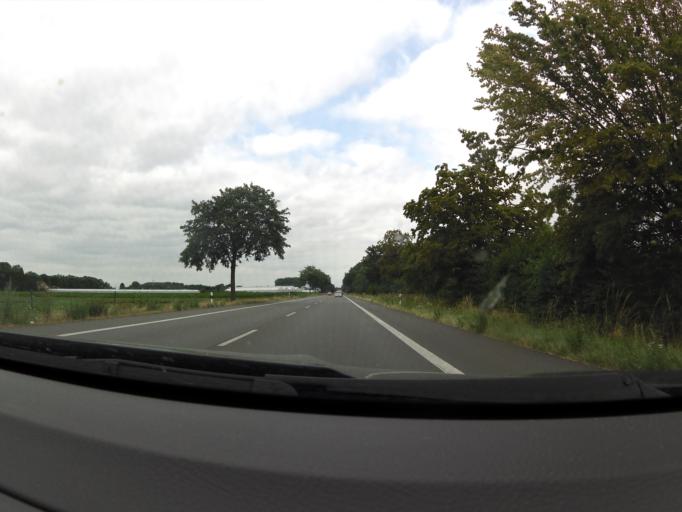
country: DE
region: North Rhine-Westphalia
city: Straelen
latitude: 51.4248
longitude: 6.2673
